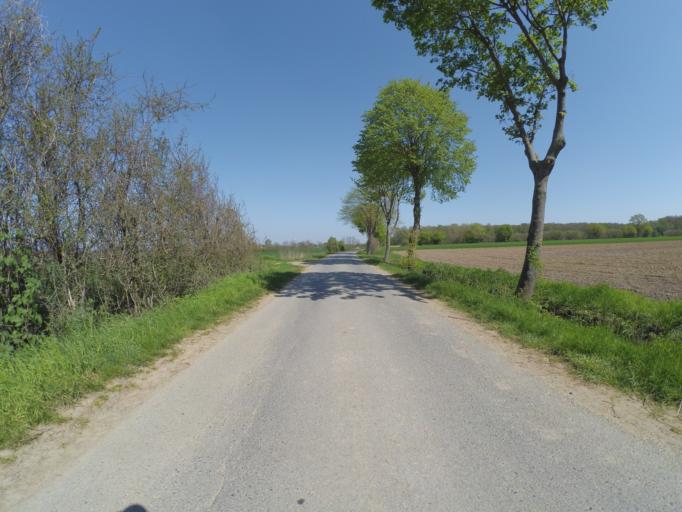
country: DE
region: North Rhine-Westphalia
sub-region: Regierungsbezirk Munster
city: Nordkirchen
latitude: 51.7701
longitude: 7.5522
